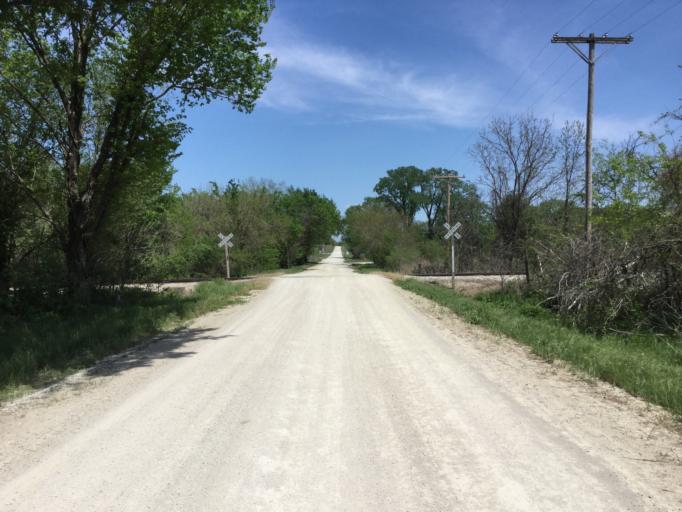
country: US
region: Kansas
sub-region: Montgomery County
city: Cherryvale
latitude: 37.3256
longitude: -95.5872
